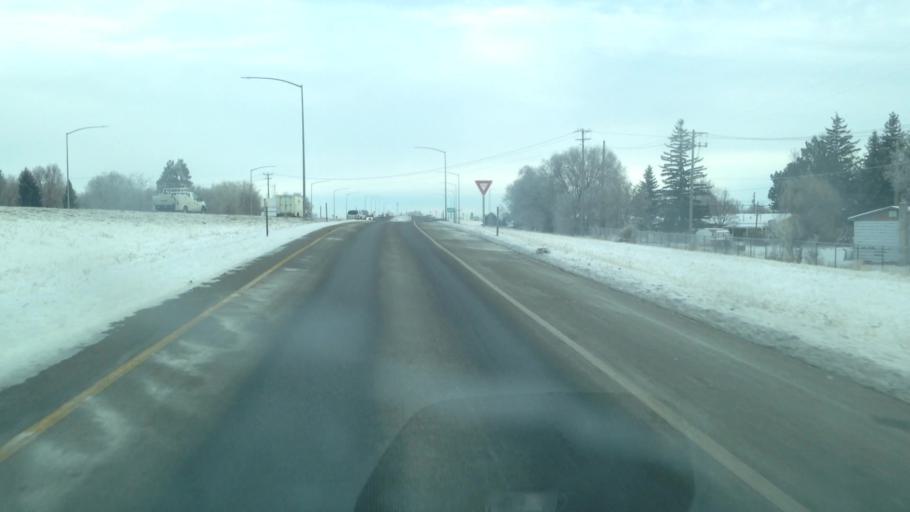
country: US
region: Idaho
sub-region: Bonneville County
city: Idaho Falls
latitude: 43.5093
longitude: -112.0454
